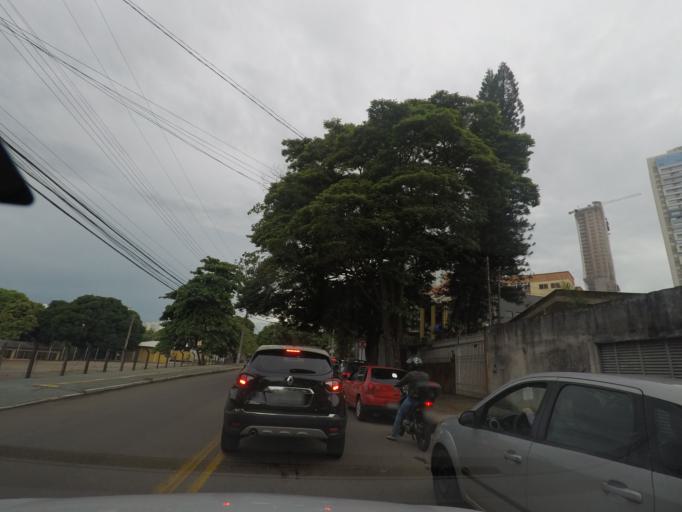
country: BR
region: Goias
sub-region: Goiania
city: Goiania
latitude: -16.7016
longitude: -49.2517
